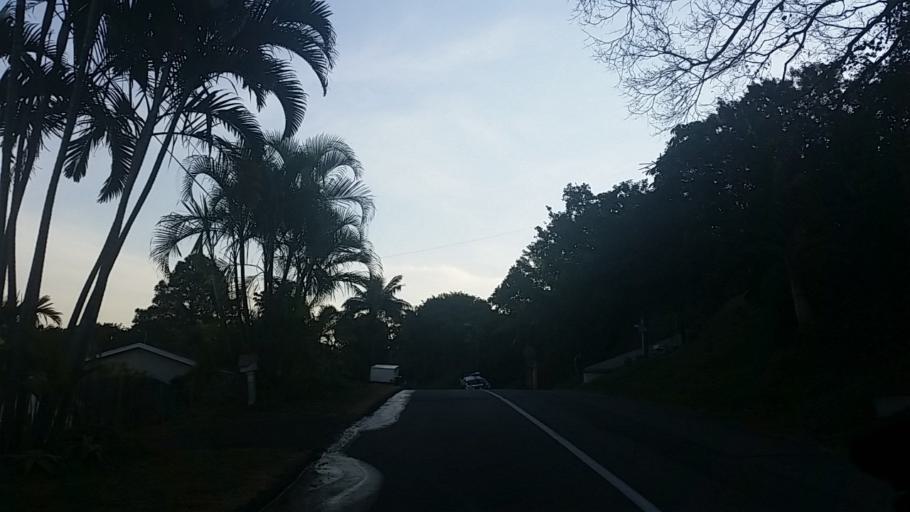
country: ZA
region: KwaZulu-Natal
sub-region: eThekwini Metropolitan Municipality
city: Berea
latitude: -29.8504
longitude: 30.9162
